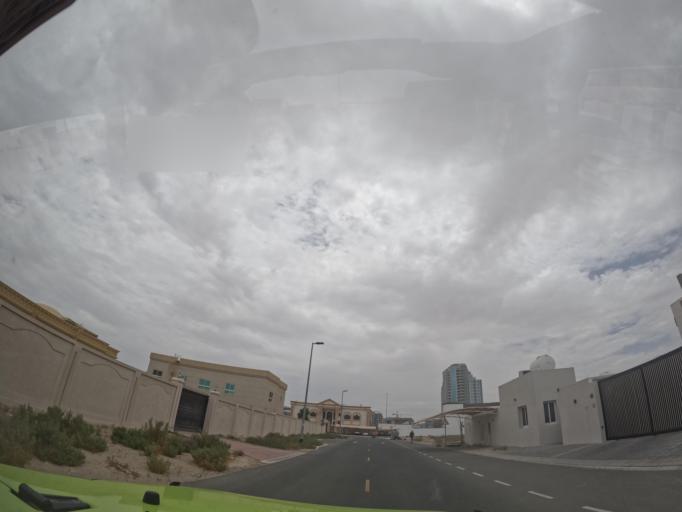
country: AE
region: Dubai
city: Dubai
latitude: 25.1271
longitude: 55.3705
